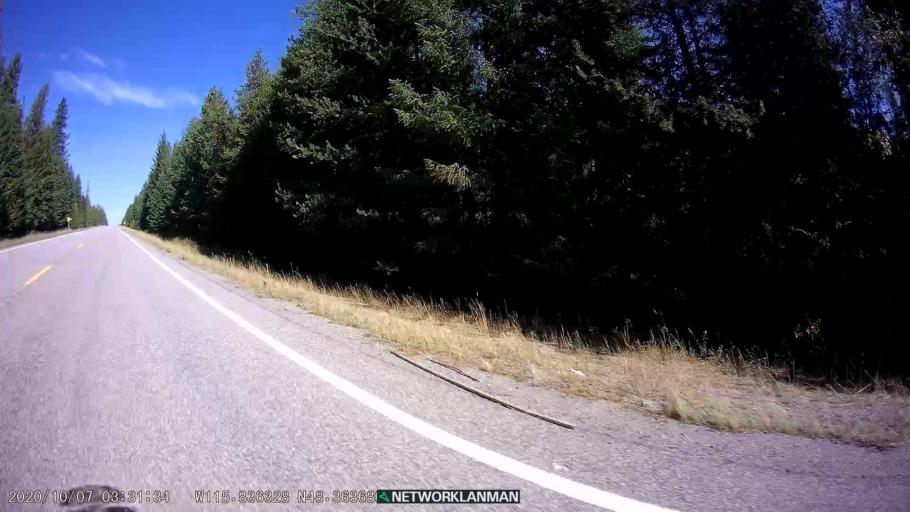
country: US
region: Montana
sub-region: Lincoln County
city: Libby
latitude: 48.3638
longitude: -115.8363
